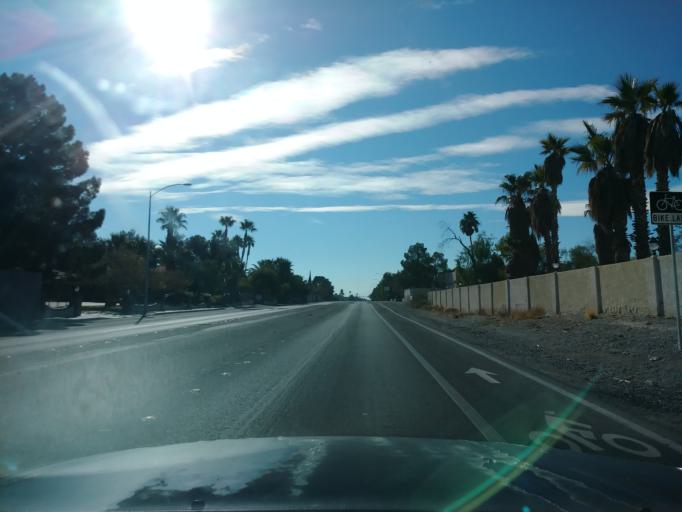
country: US
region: Nevada
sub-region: Clark County
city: Spring Valley
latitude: 36.1493
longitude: -115.2705
